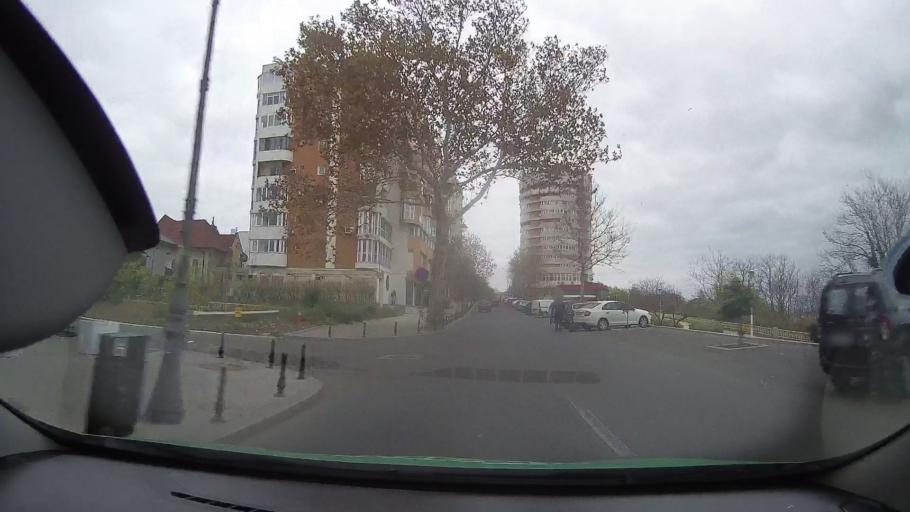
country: RO
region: Constanta
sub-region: Municipiul Constanta
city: Constanta
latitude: 44.1783
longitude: 28.6545
